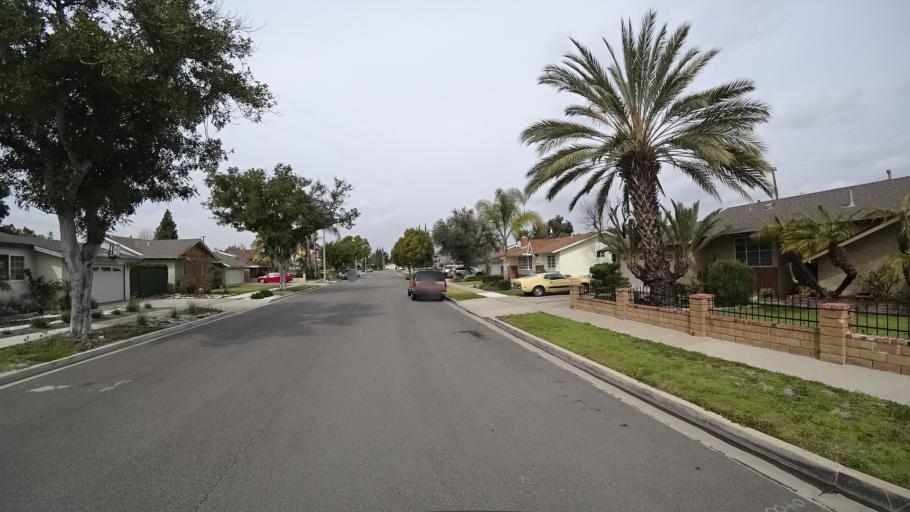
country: US
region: California
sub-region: Orange County
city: Stanton
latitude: 33.8216
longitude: -117.9772
